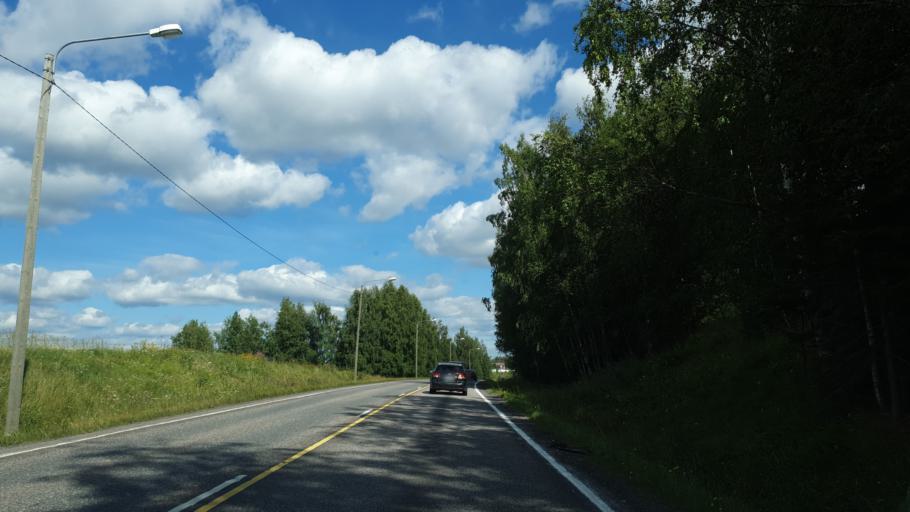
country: FI
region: Central Finland
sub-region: Jaemsae
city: Jaemsae
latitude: 61.8488
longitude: 25.1571
